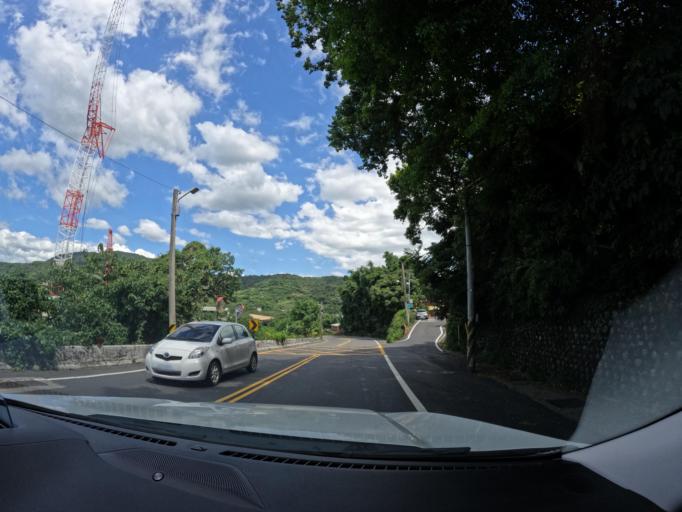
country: TW
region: Taipei
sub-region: Taipei
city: Banqiao
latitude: 25.1226
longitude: 121.3899
